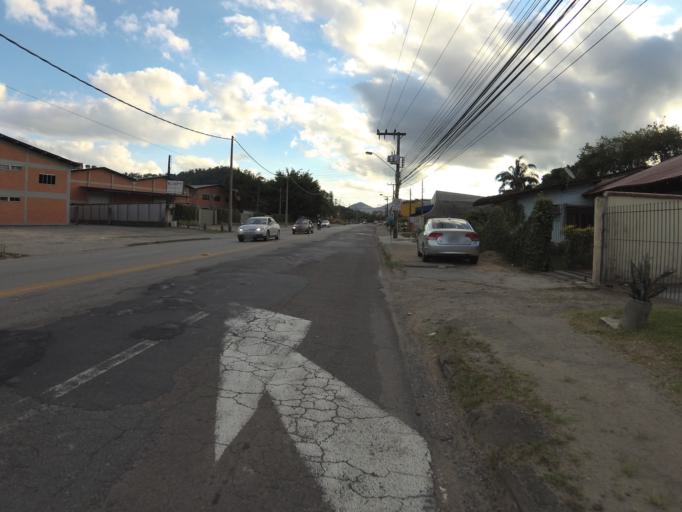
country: BR
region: Santa Catarina
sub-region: Blumenau
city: Blumenau
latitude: -26.8874
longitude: -49.1192
